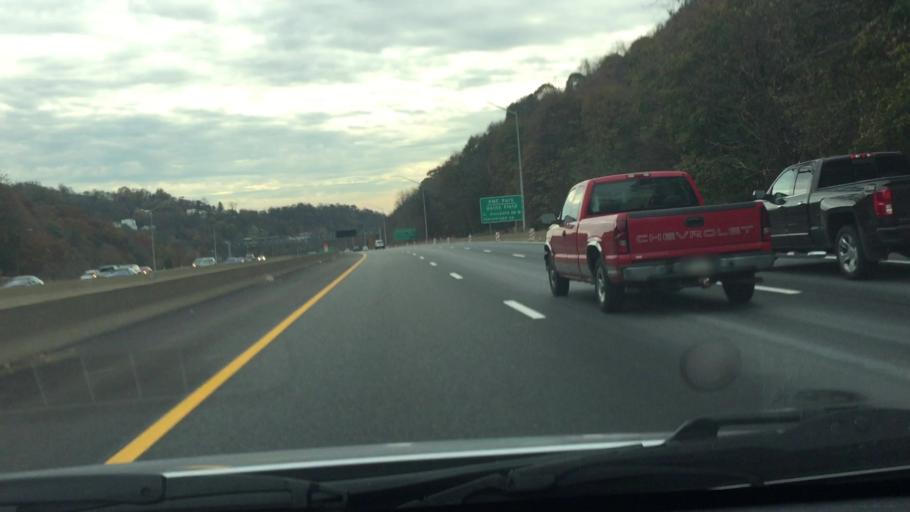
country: US
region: Pennsylvania
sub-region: Allegheny County
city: Millvale
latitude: 40.4732
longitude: -80.0056
